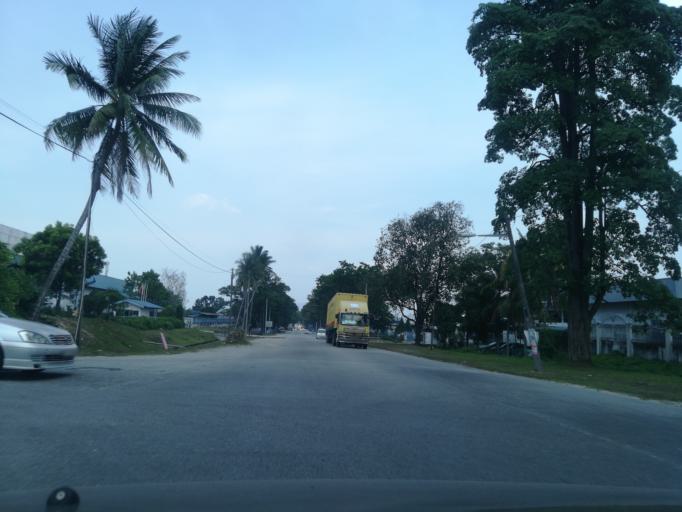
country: MY
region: Kedah
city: Kulim
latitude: 5.4122
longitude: 100.5631
